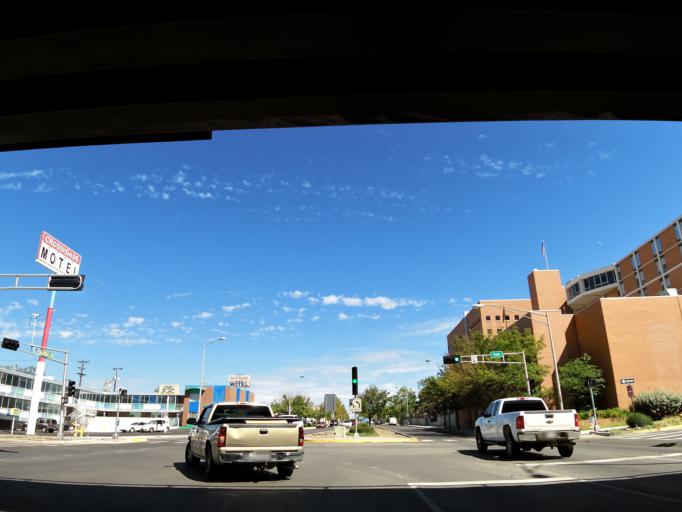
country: US
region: New Mexico
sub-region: Bernalillo County
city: Albuquerque
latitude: 35.0826
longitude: -106.6365
